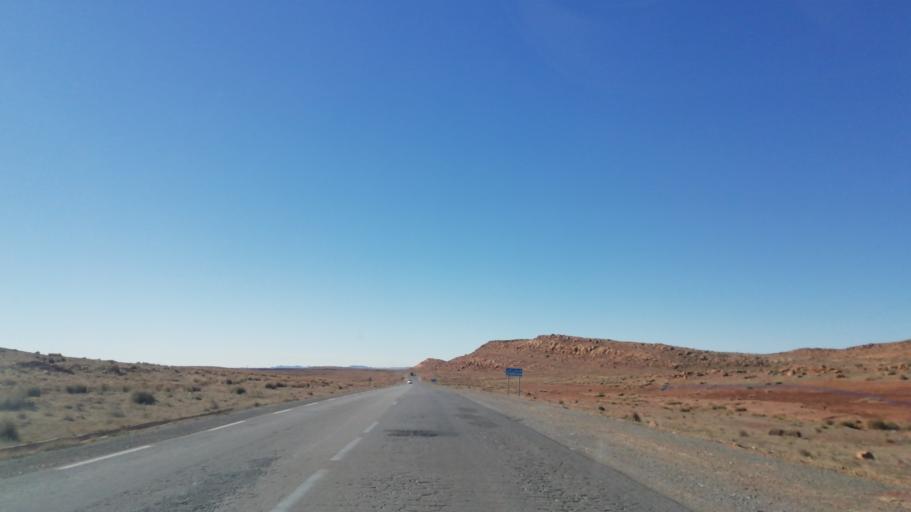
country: DZ
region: El Bayadh
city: El Bayadh
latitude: 33.6597
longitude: 1.4215
